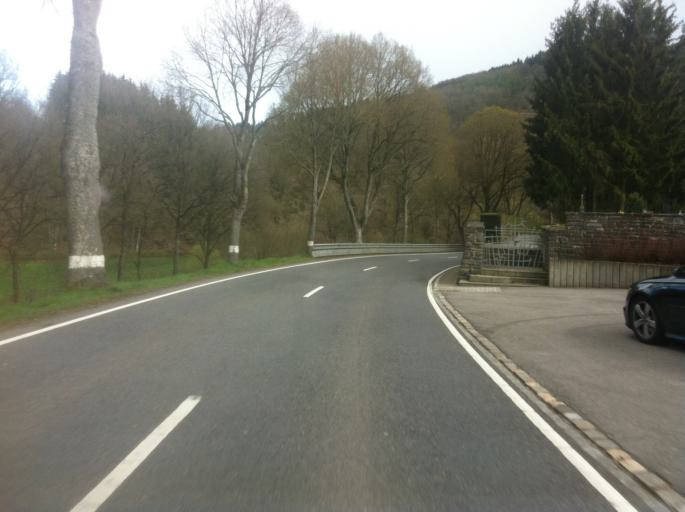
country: LU
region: Diekirch
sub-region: Canton de Wiltz
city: Eschweiler
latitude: 49.9792
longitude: 5.9542
